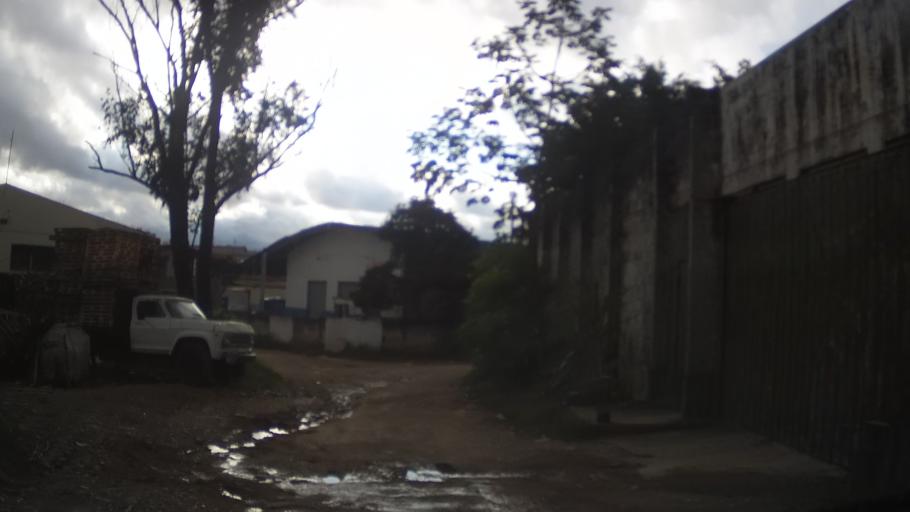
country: BR
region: Sao Paulo
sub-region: Guarulhos
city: Guarulhos
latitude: -23.4630
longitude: -46.4851
